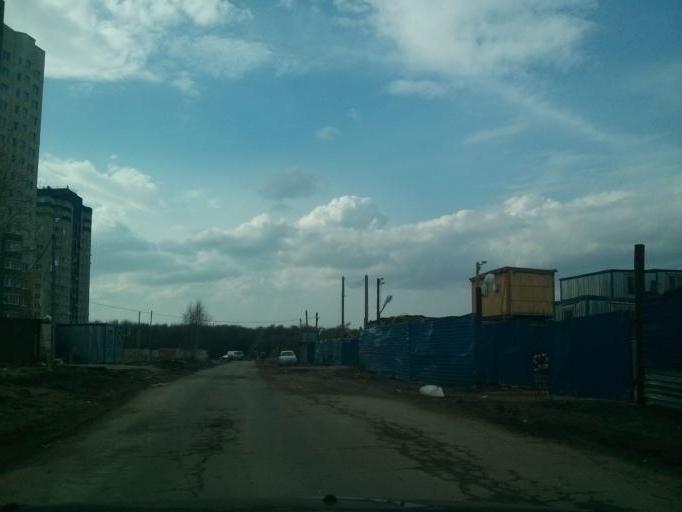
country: RU
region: Nizjnij Novgorod
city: Nizhniy Novgorod
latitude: 56.2658
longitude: 44.0206
